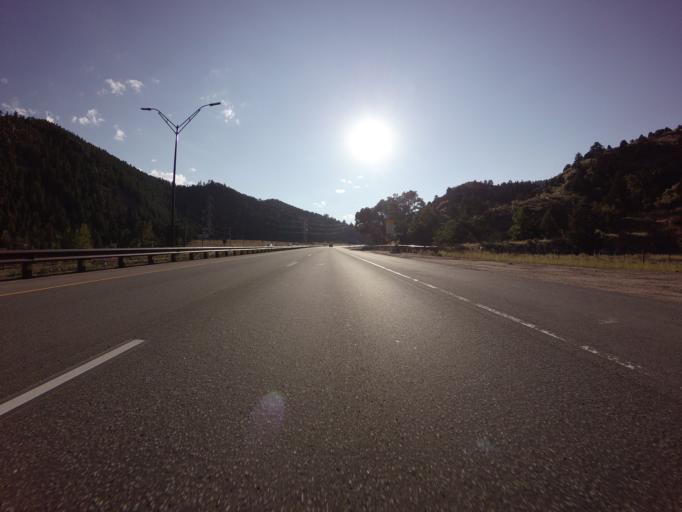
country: US
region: Colorado
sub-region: Clear Creek County
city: Idaho Springs
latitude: 39.7444
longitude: -105.4798
